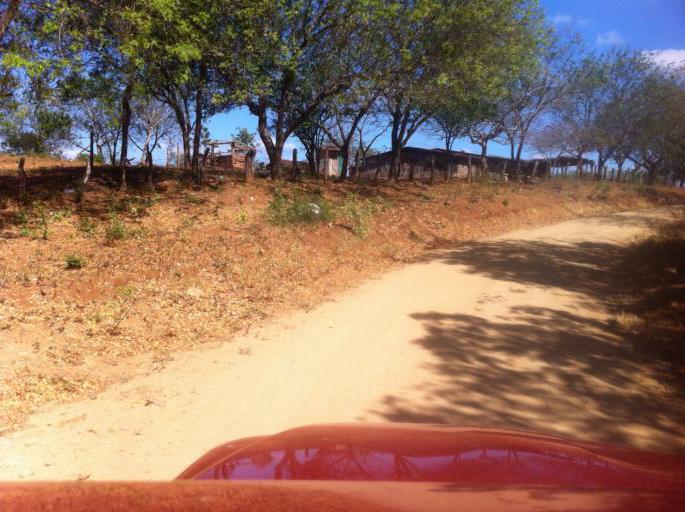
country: NI
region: Carazo
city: Santa Teresa
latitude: 11.6187
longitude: -86.3185
